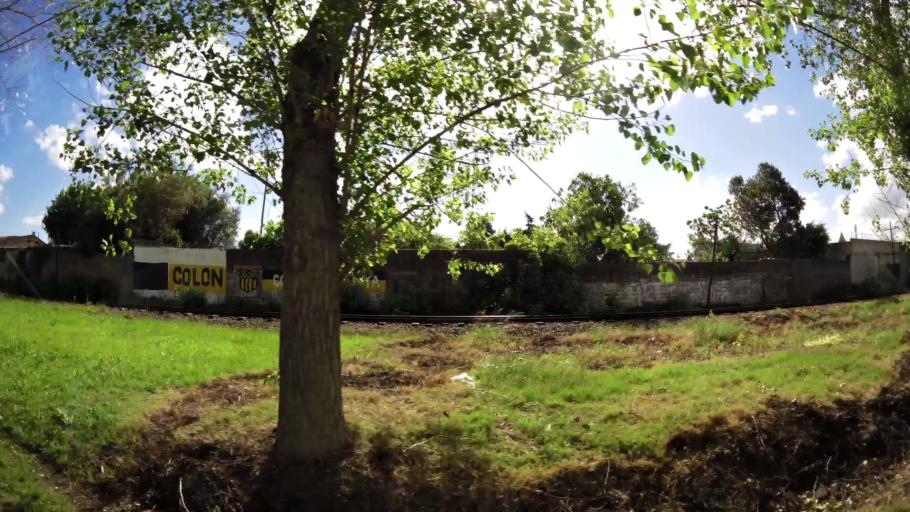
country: UY
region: Canelones
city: La Paz
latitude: -34.8095
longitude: -56.2202
